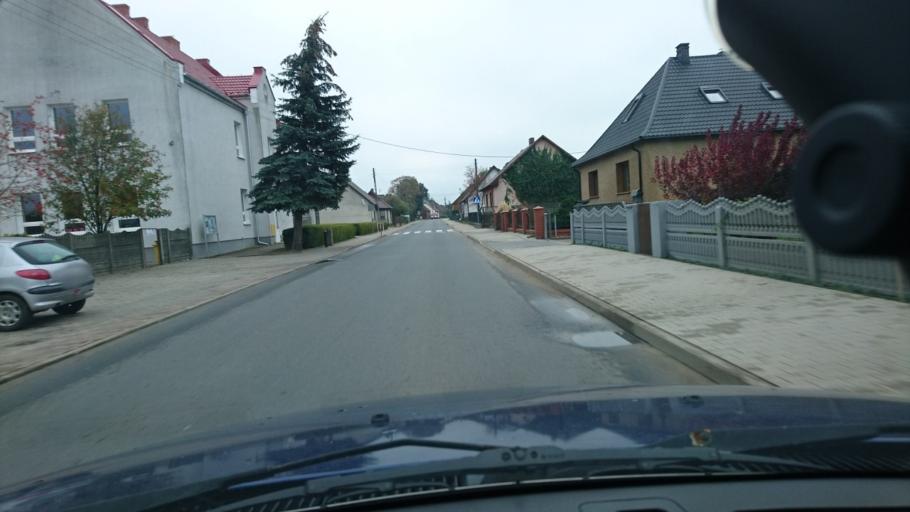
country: PL
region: Greater Poland Voivodeship
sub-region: Powiat ostrowski
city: Odolanow
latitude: 51.5740
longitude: 17.6239
